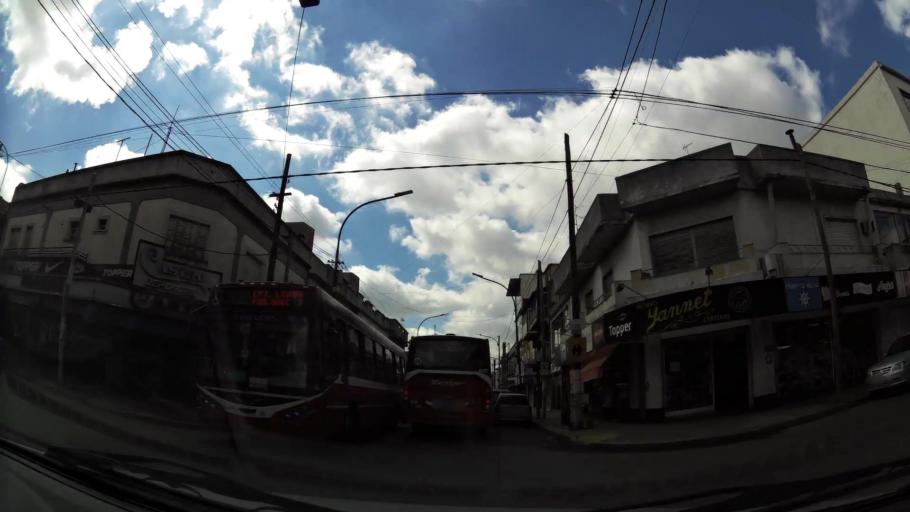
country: AR
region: Buenos Aires
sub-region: Partido de Lanus
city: Lanus
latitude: -34.6919
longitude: -58.4068
